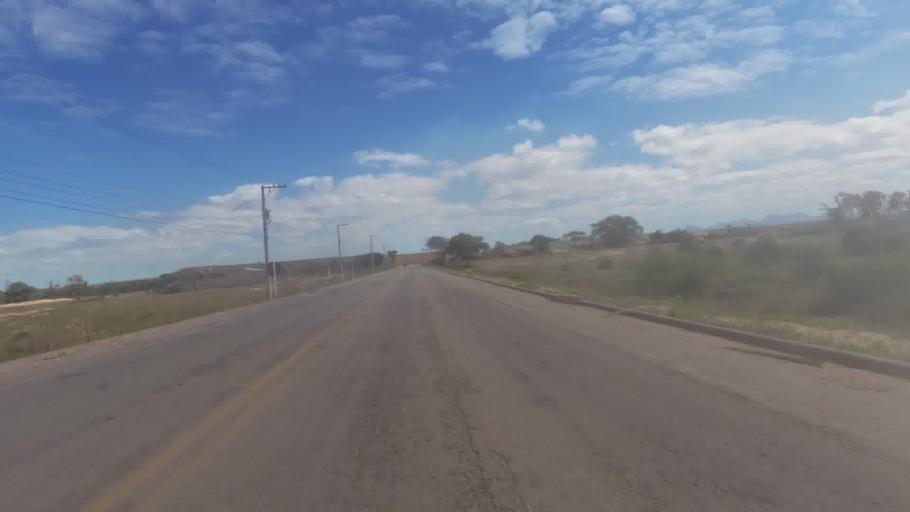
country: BR
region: Espirito Santo
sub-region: Marataizes
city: Marataizes
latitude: -21.1882
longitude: -40.9362
